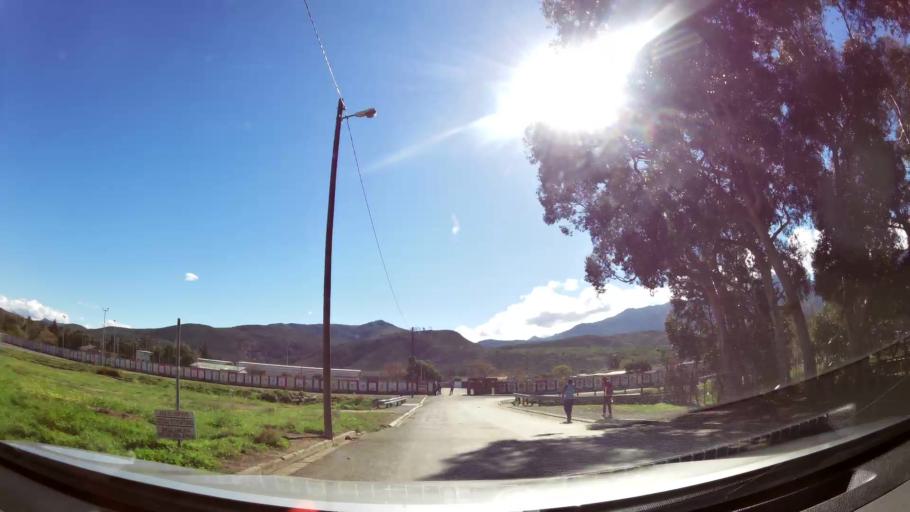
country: ZA
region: Western Cape
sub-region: Cape Winelands District Municipality
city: Ashton
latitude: -33.7941
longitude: 19.8811
